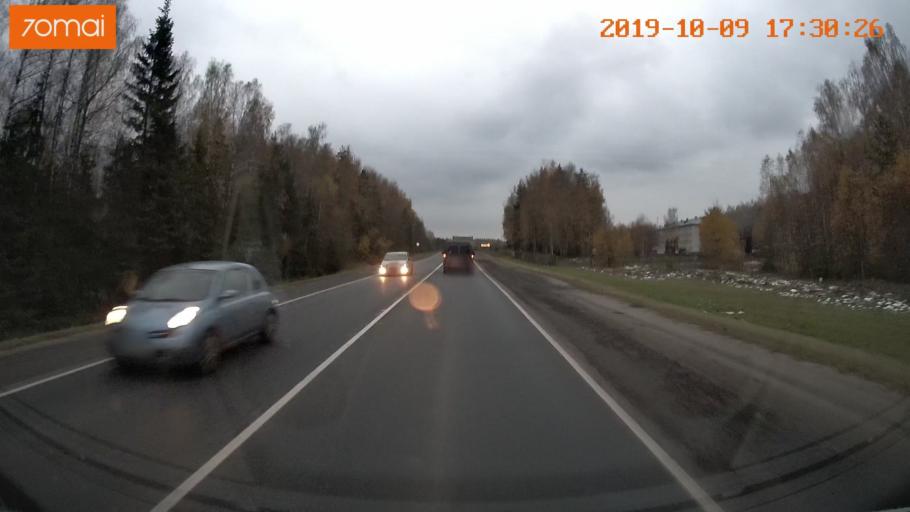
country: RU
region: Ivanovo
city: Bogorodskoye
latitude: 57.1428
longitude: 41.0494
